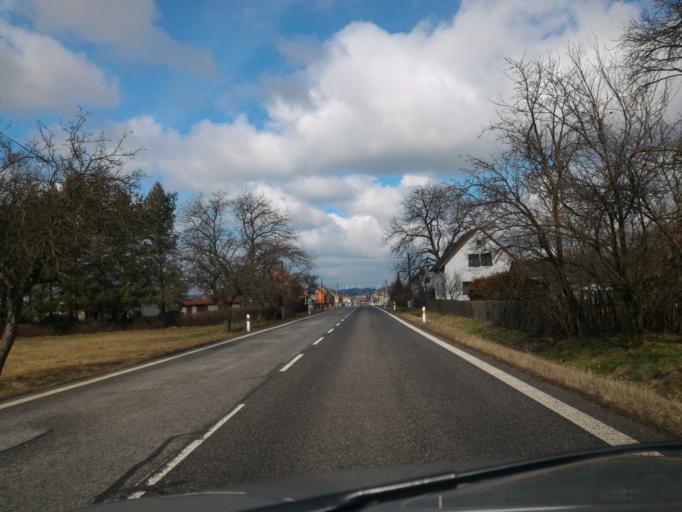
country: PL
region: Silesian Voivodeship
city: Zawidow
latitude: 51.0122
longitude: 15.0678
